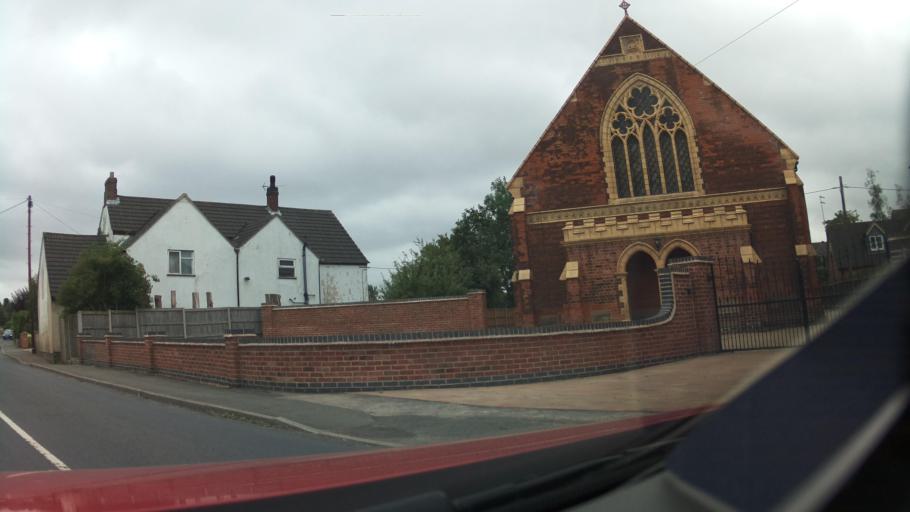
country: GB
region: England
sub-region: Derbyshire
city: Swadlincote
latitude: 52.7877
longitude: -1.5226
